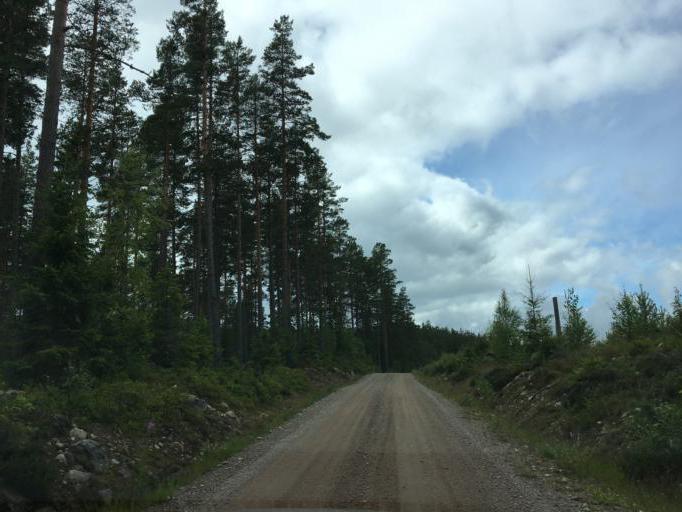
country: SE
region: OErebro
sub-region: Hallefors Kommun
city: Haellefors
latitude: 60.0690
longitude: 14.4877
